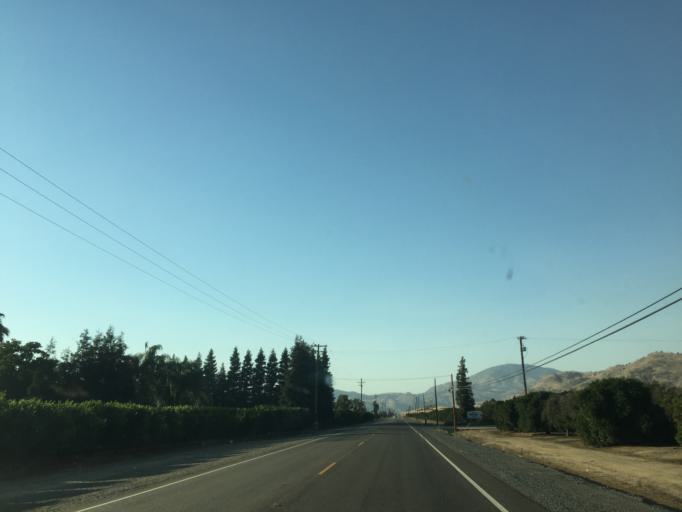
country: US
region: California
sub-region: Fresno County
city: Orange Cove
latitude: 36.6503
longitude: -119.3047
